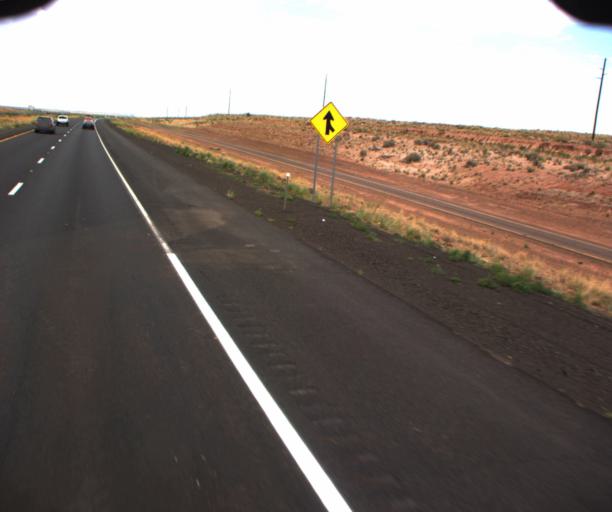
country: US
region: Arizona
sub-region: Navajo County
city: Winslow
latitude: 34.9759
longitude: -110.5266
